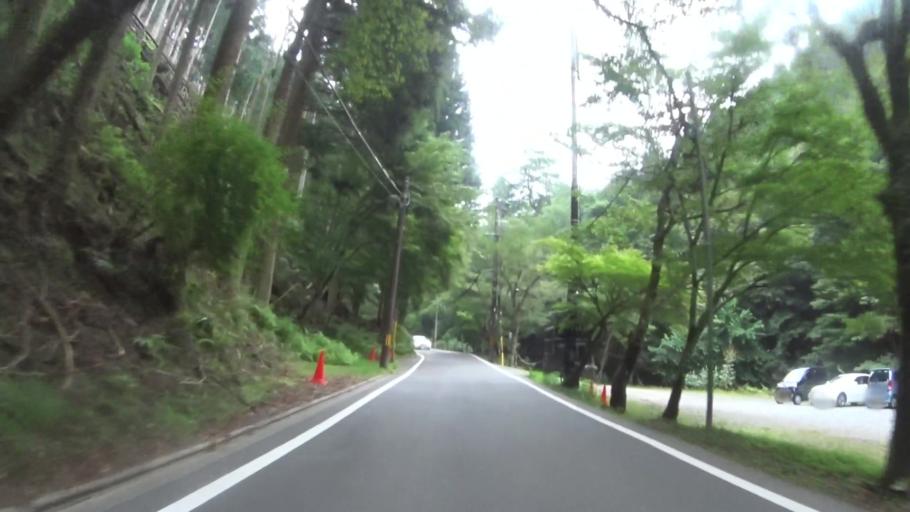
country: JP
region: Kyoto
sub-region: Kyoto-shi
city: Kamigyo-ku
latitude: 35.1154
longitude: 135.7605
